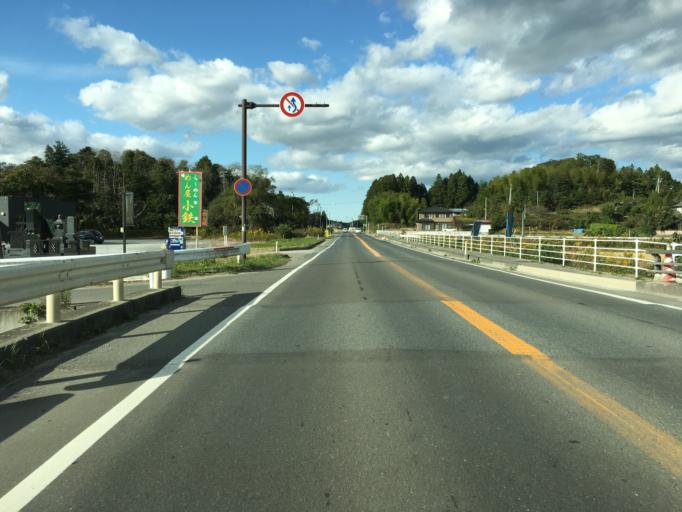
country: JP
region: Miyagi
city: Marumori
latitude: 37.8826
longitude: 140.9144
